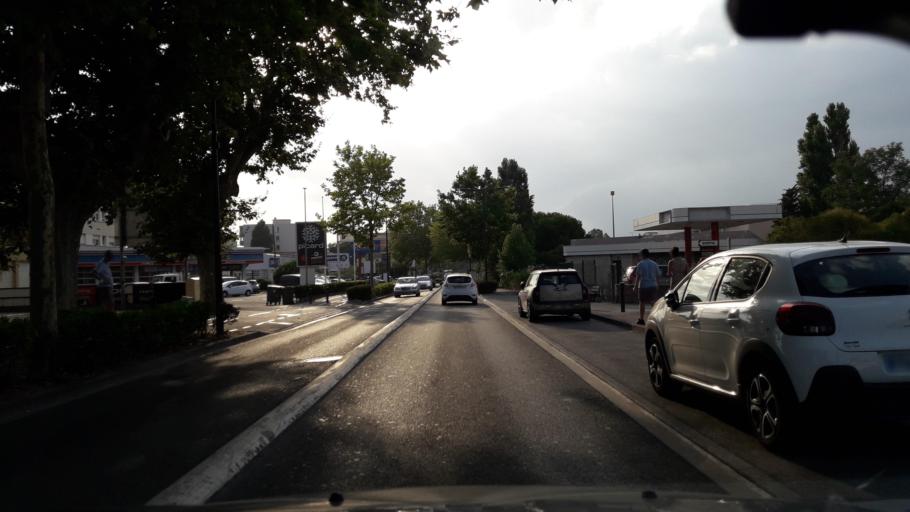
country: FR
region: Provence-Alpes-Cote d'Azur
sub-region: Departement du Var
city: Saint-Raphael
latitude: 43.4306
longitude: 6.7560
